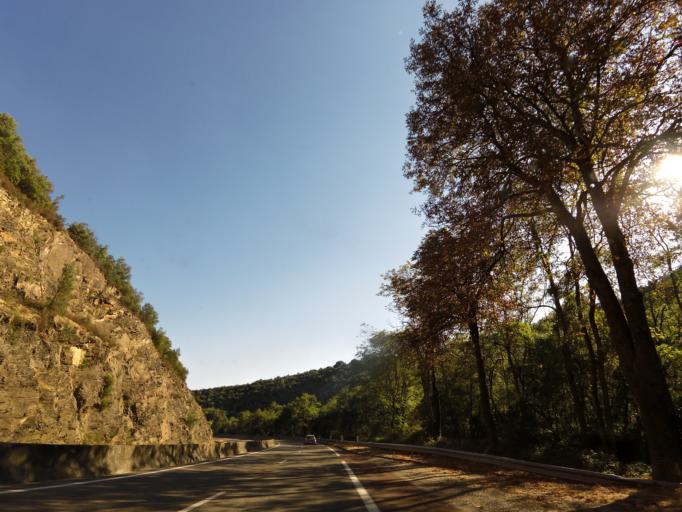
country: FR
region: Languedoc-Roussillon
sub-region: Departement du Gard
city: Sumene
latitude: 43.9850
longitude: 3.6854
